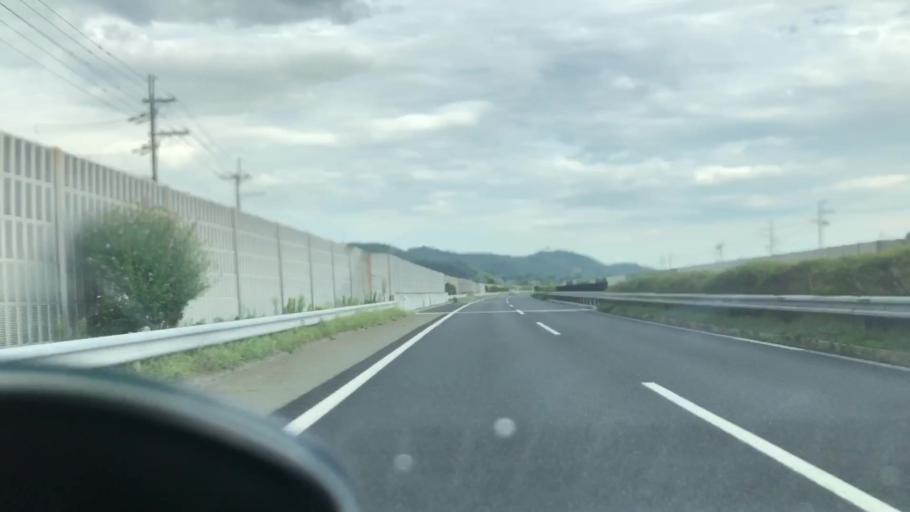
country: JP
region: Hyogo
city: Ono
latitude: 34.9391
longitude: 134.8280
